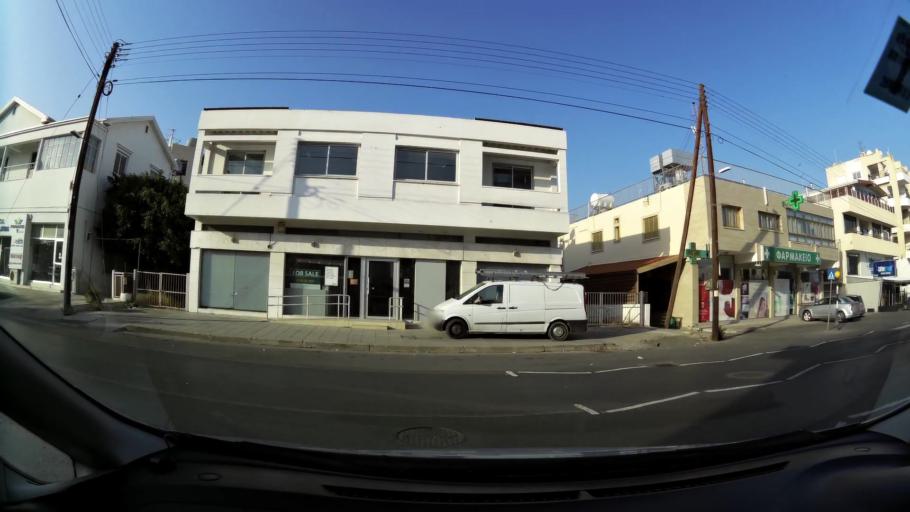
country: CY
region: Lefkosia
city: Nicosia
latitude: 35.1712
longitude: 33.3361
